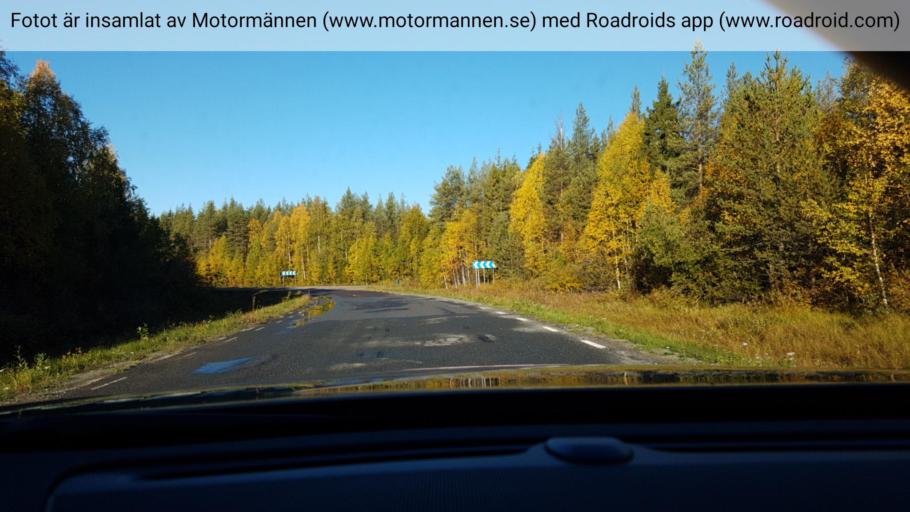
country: SE
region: Norrbotten
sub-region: Bodens Kommun
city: Boden
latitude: 66.0603
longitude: 21.4265
